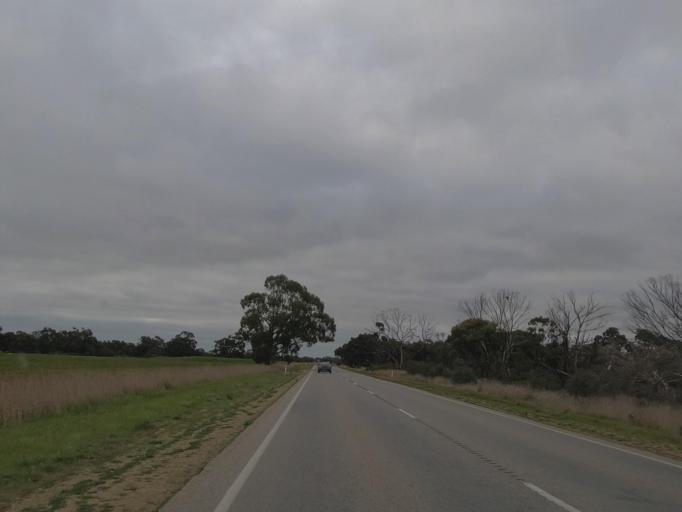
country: AU
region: Victoria
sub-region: Greater Bendigo
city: Long Gully
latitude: -36.2207
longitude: 143.9556
